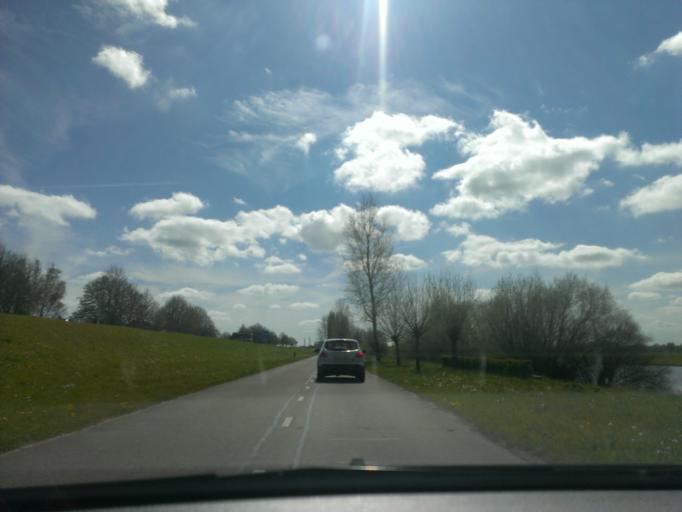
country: NL
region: Overijssel
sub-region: Gemeente Olst-Wijhe
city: Wijhe
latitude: 52.3897
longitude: 6.1287
